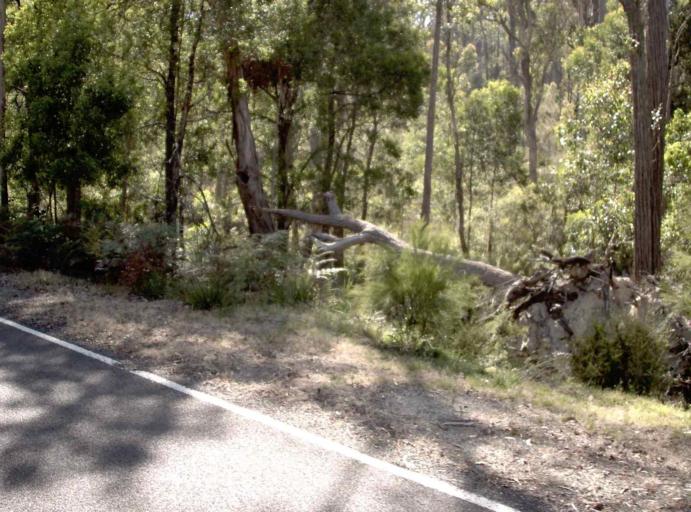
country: AU
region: New South Wales
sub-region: Bombala
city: Bombala
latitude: -37.3833
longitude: 148.6541
